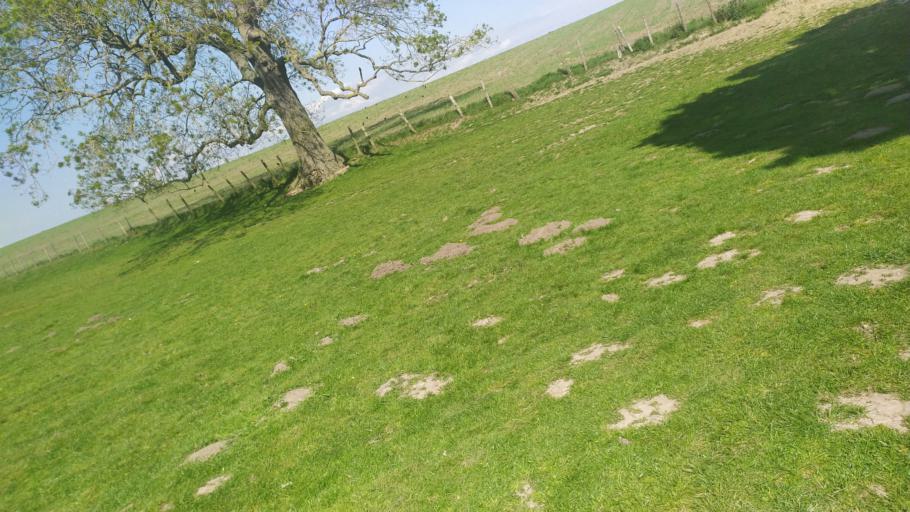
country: GB
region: England
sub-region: City and Borough of Leeds
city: Chapel Allerton
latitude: 53.8662
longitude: -1.5602
